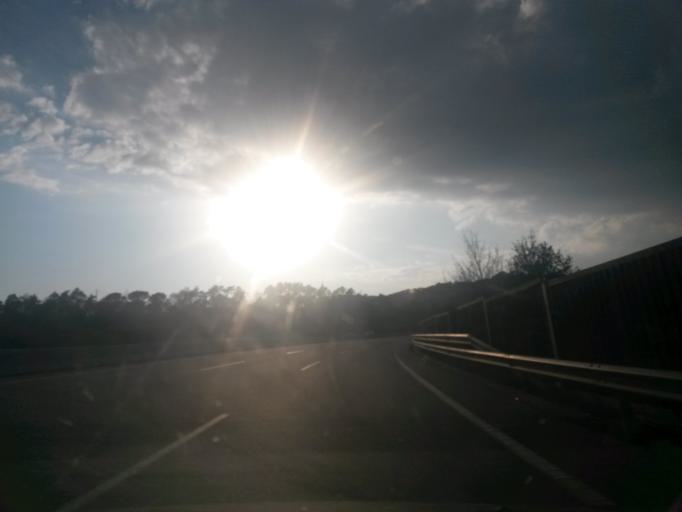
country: ES
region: Catalonia
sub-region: Provincia de Barcelona
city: Sant Julia de Vilatorta
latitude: 41.8914
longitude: 2.3579
